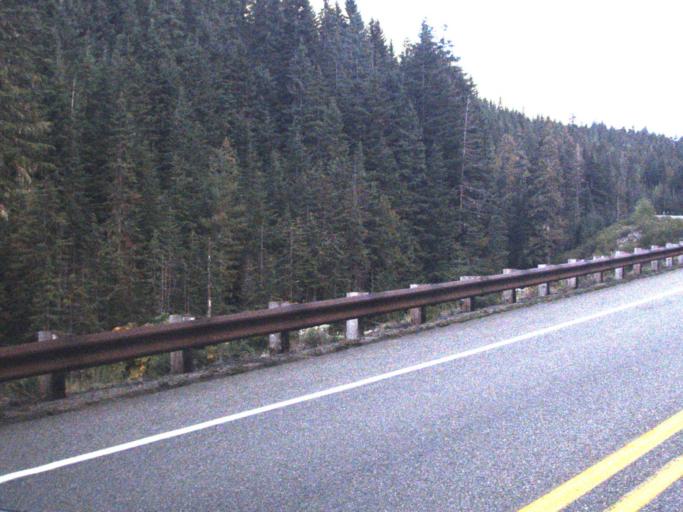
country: US
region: Washington
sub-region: Snohomish County
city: Darrington
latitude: 48.6306
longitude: -120.8455
